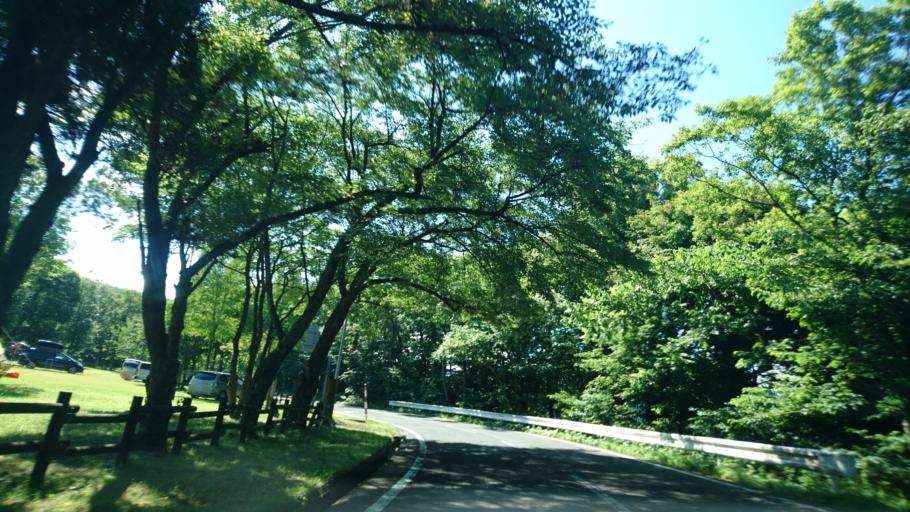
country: JP
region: Akita
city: Kakunodatemachi
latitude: 39.7445
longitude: 140.6835
